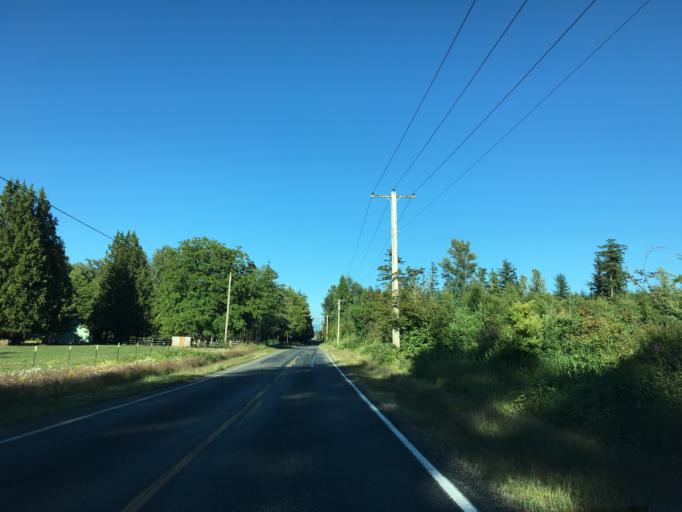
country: US
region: Washington
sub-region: Whatcom County
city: Ferndale
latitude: 48.9135
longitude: -122.6256
